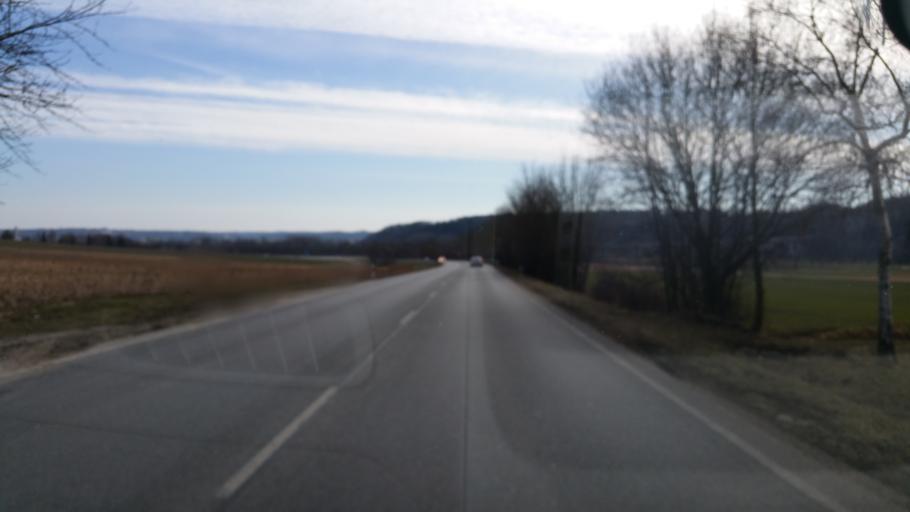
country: DE
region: Bavaria
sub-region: Lower Bavaria
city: Weihmichl
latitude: 48.5731
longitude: 12.0868
